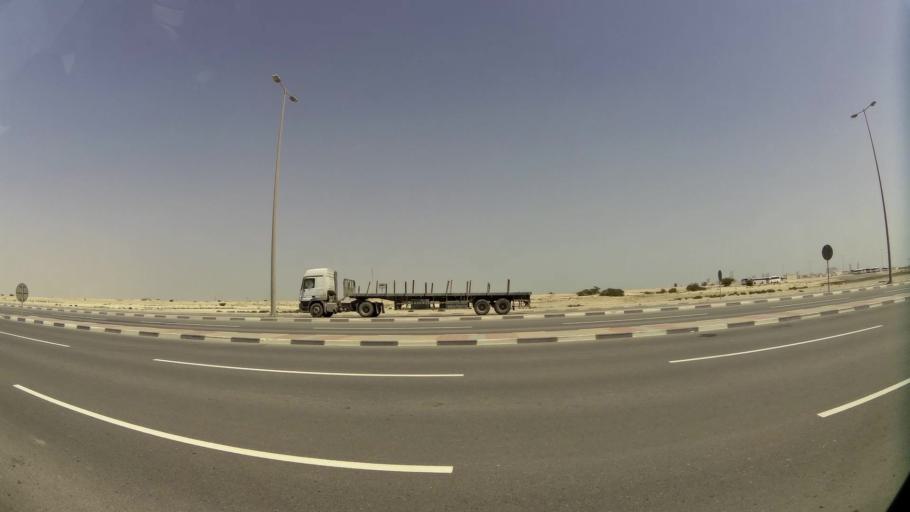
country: QA
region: Baladiyat Umm Salal
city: Umm Salal Muhammad
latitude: 25.3917
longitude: 51.4639
